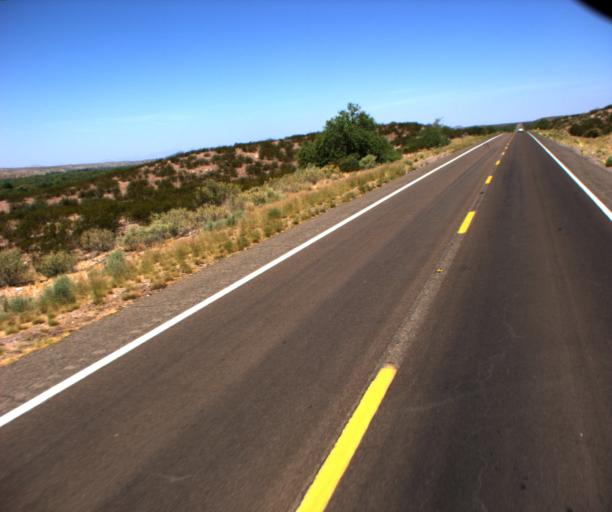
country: US
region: Arizona
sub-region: Graham County
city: Bylas
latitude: 33.1845
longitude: -110.1591
